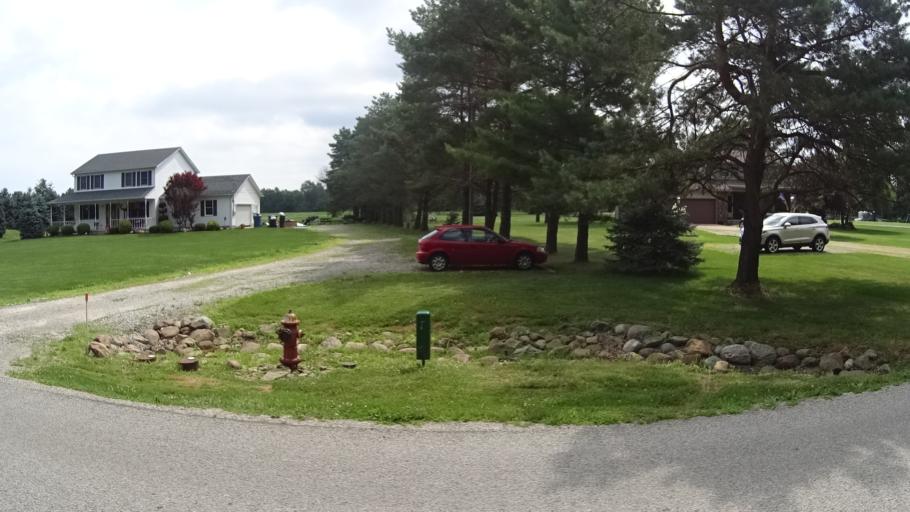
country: US
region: Ohio
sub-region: Lorain County
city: Vermilion
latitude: 41.3968
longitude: -82.4191
